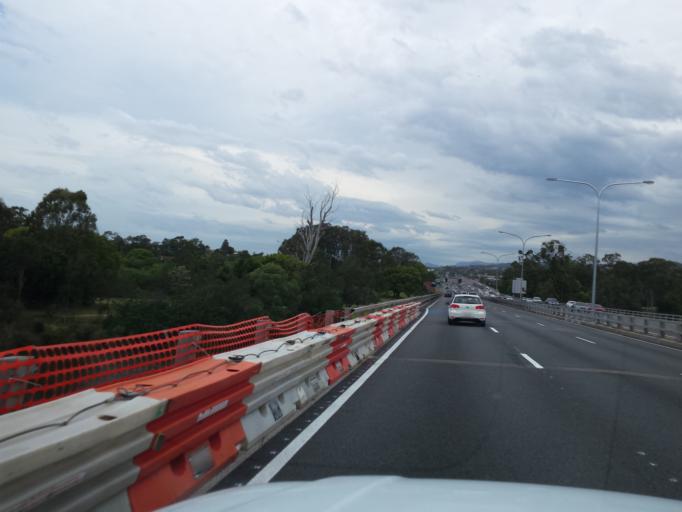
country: AU
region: Queensland
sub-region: Gold Coast
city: Nerang
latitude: -27.9862
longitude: 153.3413
